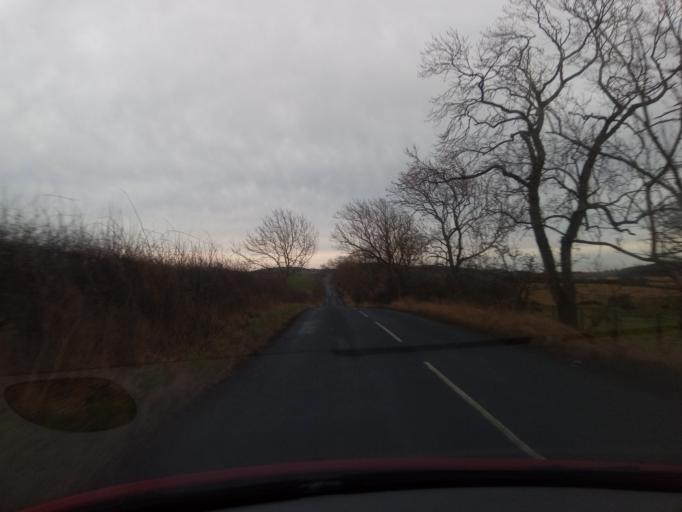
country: GB
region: England
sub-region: Northumberland
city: Ellingham
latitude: 55.4609
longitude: -1.7938
